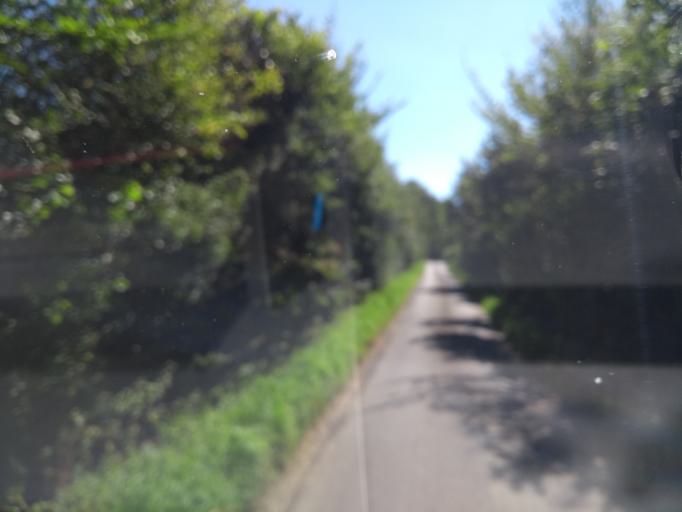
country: GB
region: England
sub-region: Somerset
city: Ilchester
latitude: 51.0546
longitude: -2.6860
